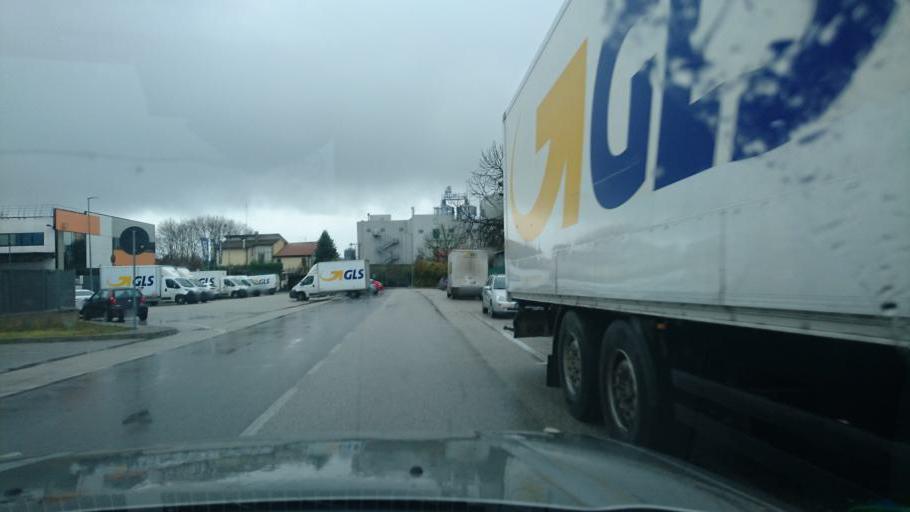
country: IT
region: Veneto
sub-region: Provincia di Padova
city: Villatora
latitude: 45.3864
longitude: 11.9579
